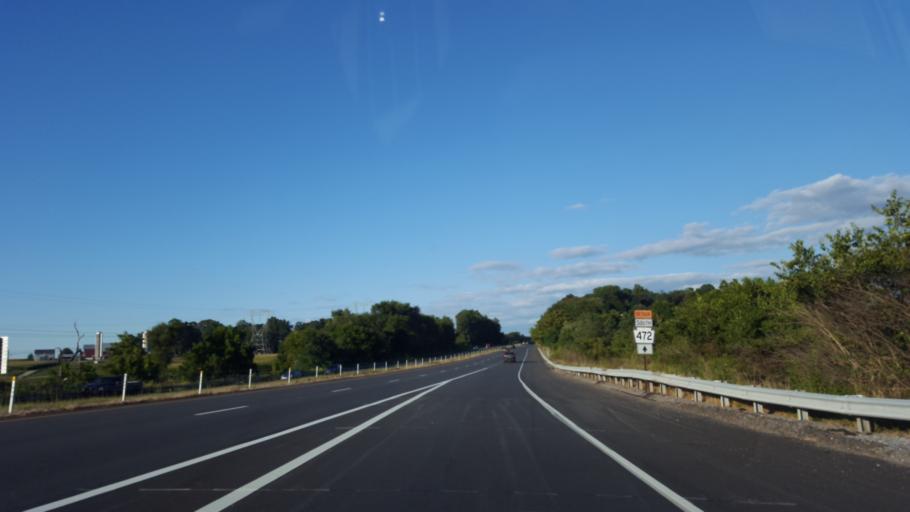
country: US
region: Pennsylvania
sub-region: Chester County
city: Oxford
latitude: 39.7904
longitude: -75.9935
